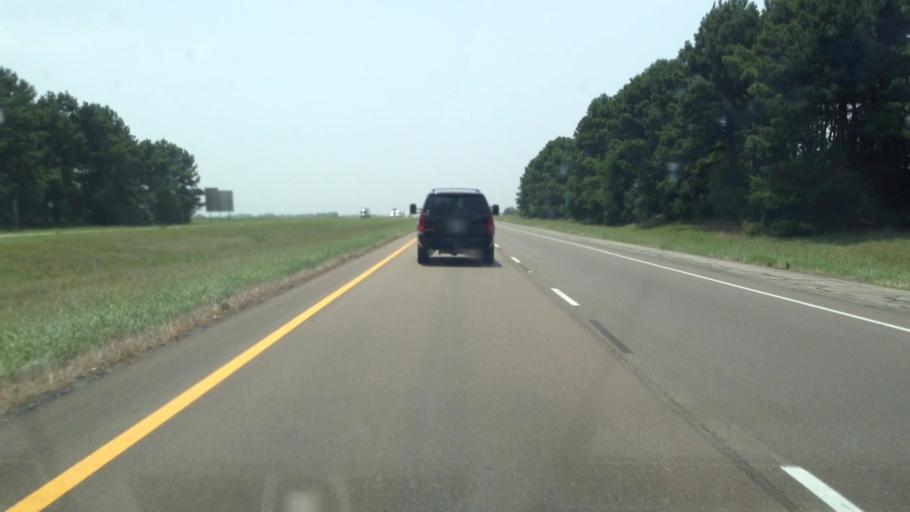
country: US
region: Texas
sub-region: Morris County
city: Omaha
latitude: 33.2919
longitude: -94.7620
